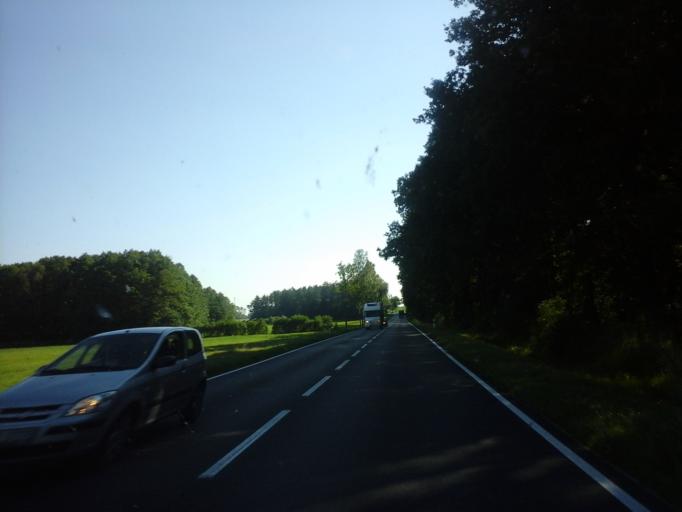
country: PL
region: West Pomeranian Voivodeship
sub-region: Powiat gryficki
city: Ploty
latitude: 53.7609
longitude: 15.2310
